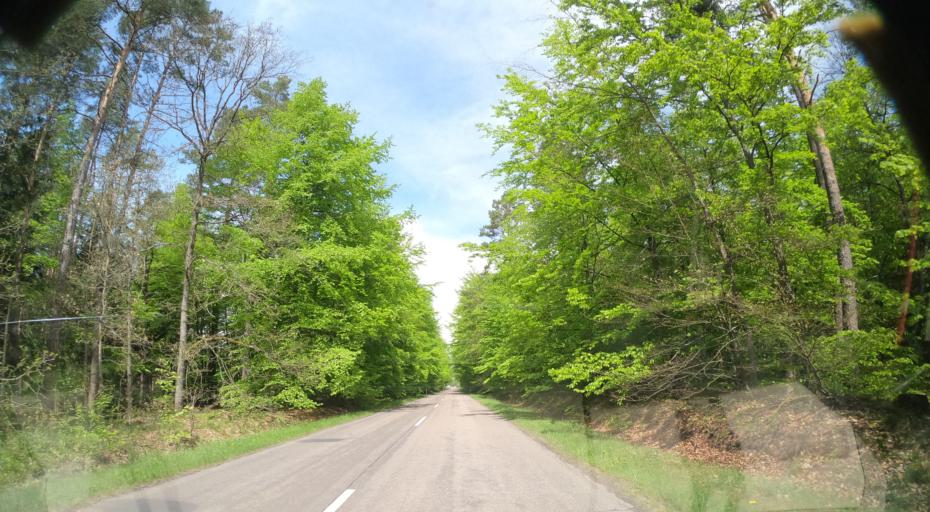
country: PL
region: West Pomeranian Voivodeship
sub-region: Powiat bialogardzki
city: Tychowo
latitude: 54.0594
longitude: 16.3010
